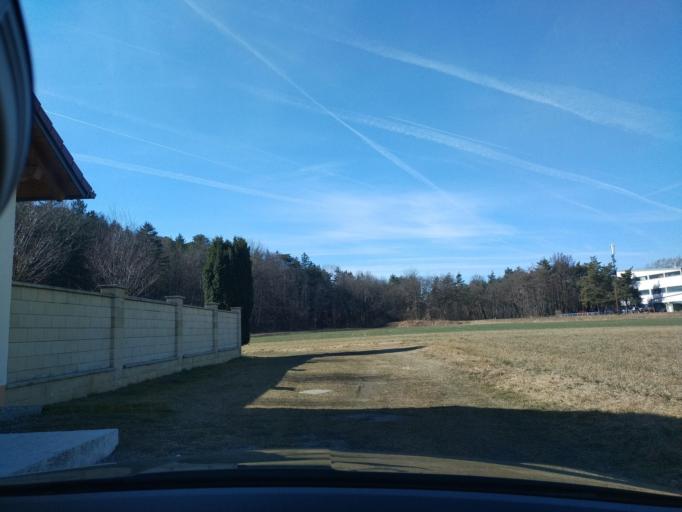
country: AT
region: Lower Austria
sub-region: Politischer Bezirk Neunkirchen
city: Pitten
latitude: 47.7247
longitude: 16.1670
